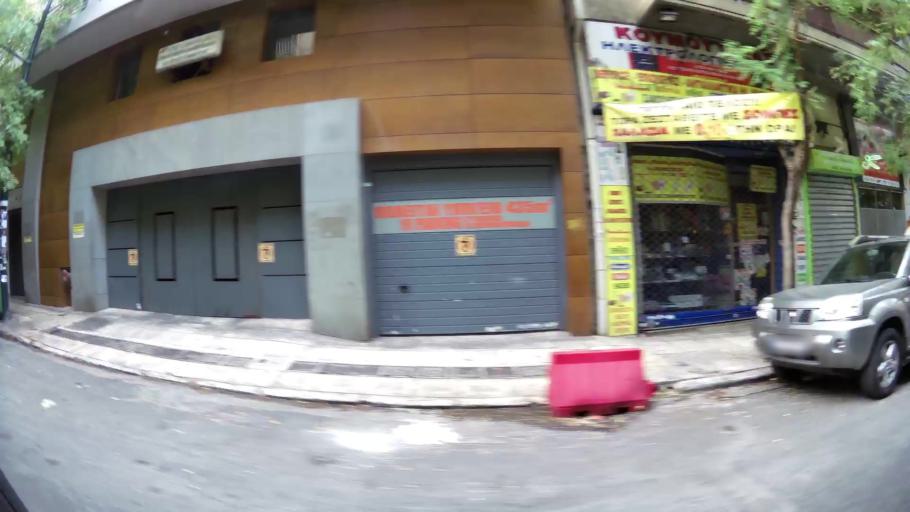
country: GR
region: Attica
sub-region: Nomarchia Athinas
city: Kipseli
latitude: 38.0009
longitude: 23.7265
